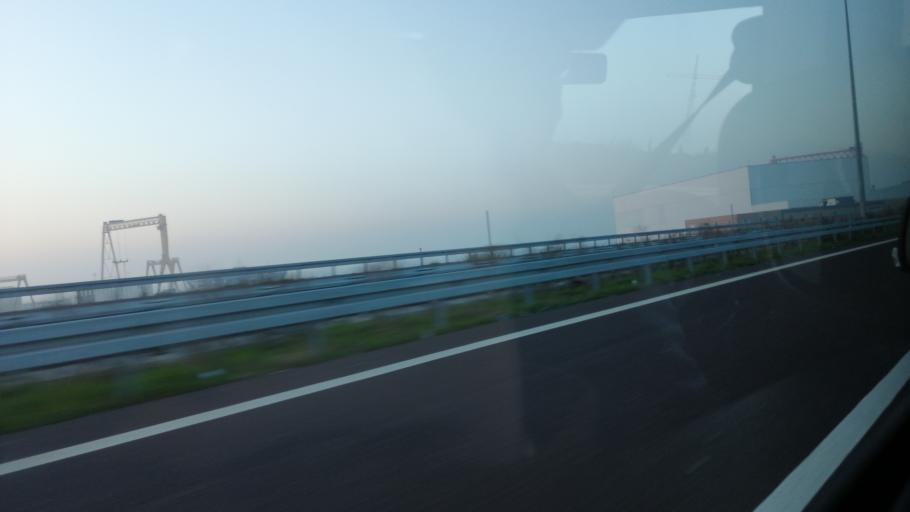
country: TR
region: Yalova
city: Altinova
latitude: 40.7245
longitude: 29.5034
